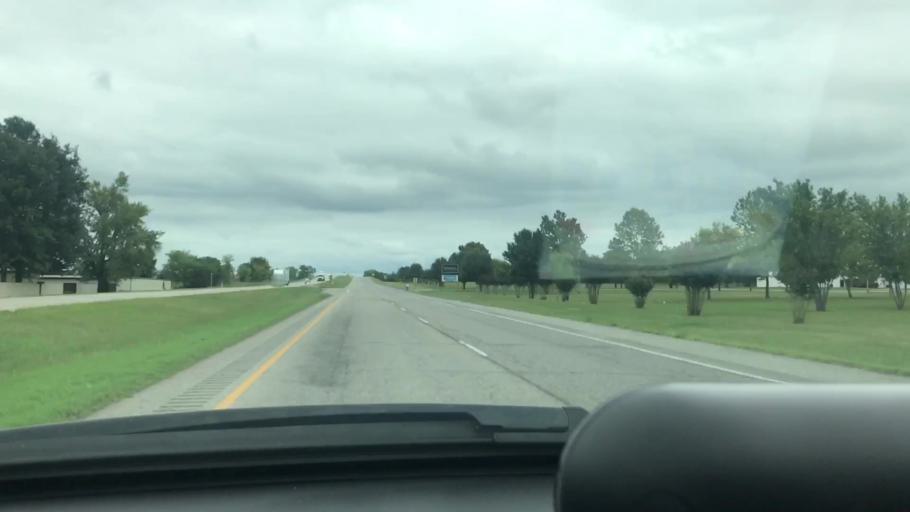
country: US
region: Oklahoma
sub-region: Wagoner County
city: Wagoner
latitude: 35.9737
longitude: -95.3853
